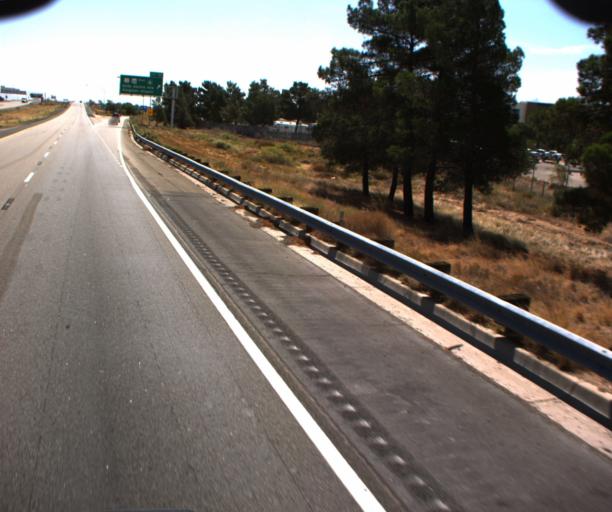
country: US
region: Arizona
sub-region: Mohave County
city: Kingman
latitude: 35.2169
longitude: -114.0159
